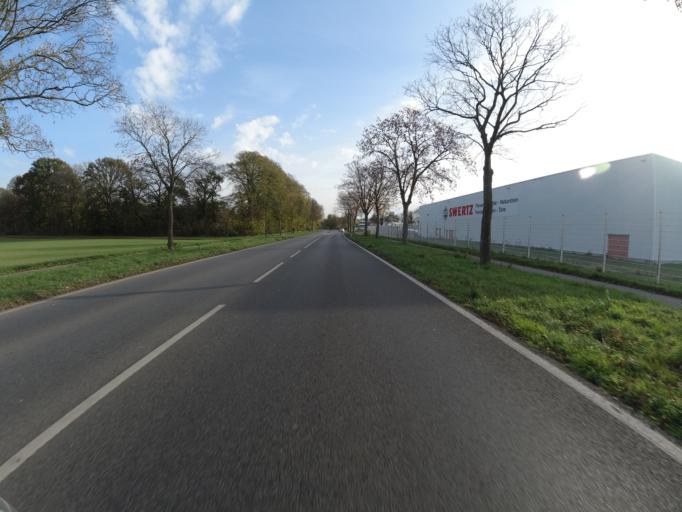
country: DE
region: North Rhine-Westphalia
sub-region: Regierungsbezirk Dusseldorf
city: Moers
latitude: 51.4644
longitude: 6.6170
